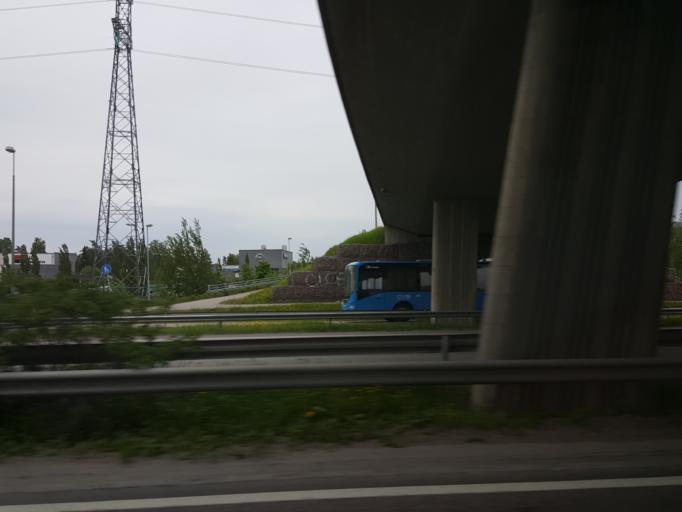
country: FI
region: Uusimaa
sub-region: Helsinki
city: Vantaa
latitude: 60.2947
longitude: 24.9838
